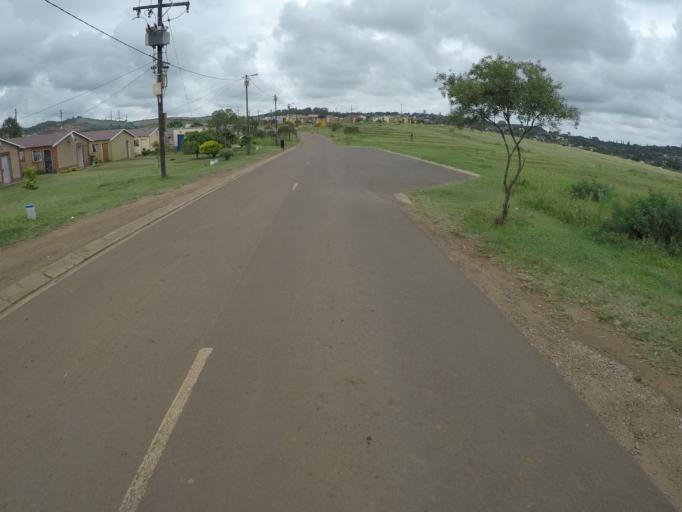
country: ZA
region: KwaZulu-Natal
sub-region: uThungulu District Municipality
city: Empangeni
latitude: -28.7678
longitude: 31.8797
